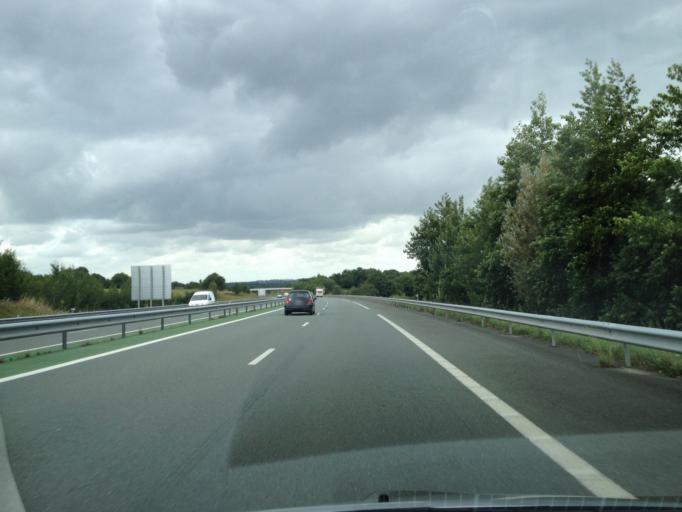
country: FR
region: Pays de la Loire
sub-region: Departement de la Vendee
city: Chambretaud
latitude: 46.9472
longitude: -0.9485
